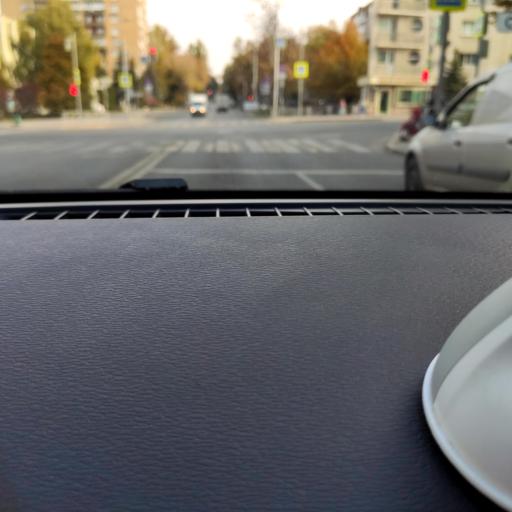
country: RU
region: Samara
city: Samara
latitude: 53.2071
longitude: 50.1210
